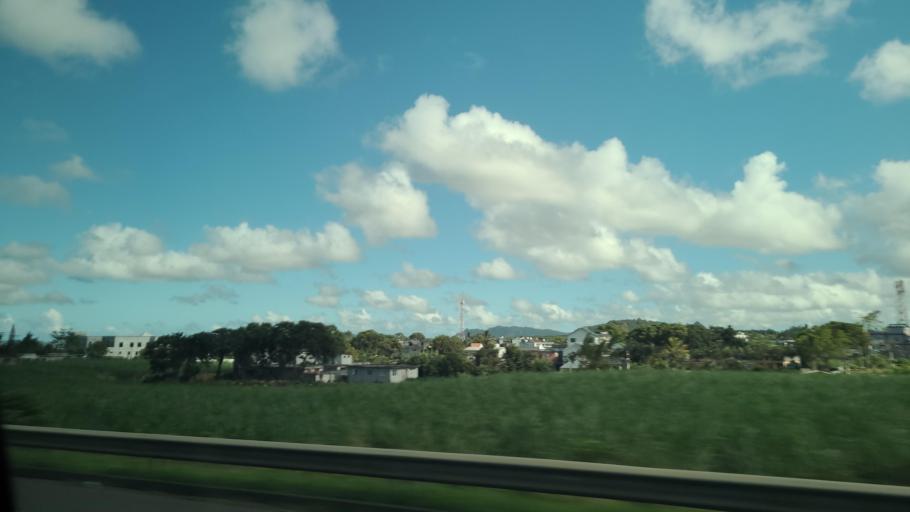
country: MU
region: Moka
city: Quartier Militaire
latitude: -20.2428
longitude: 57.5993
